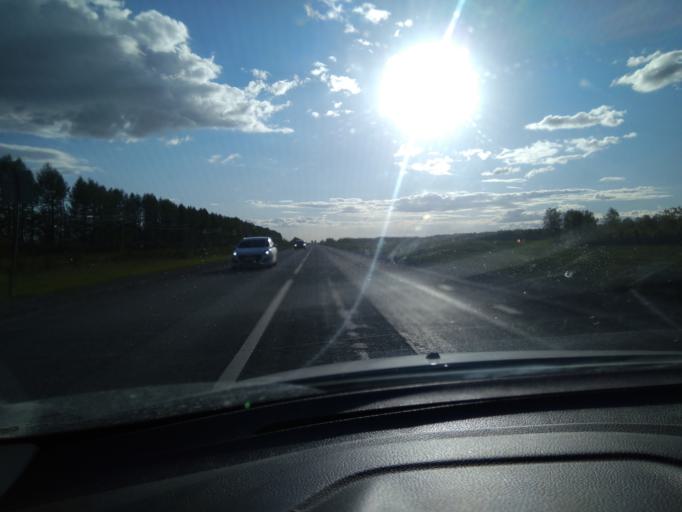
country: RU
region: Sverdlovsk
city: Troitskiy
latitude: 57.0866
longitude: 63.7285
